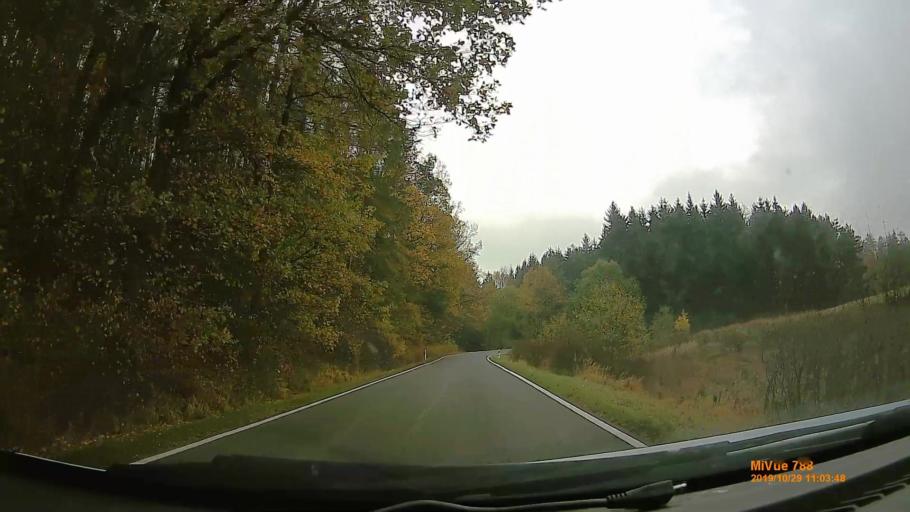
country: PL
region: Lower Silesian Voivodeship
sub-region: Powiat klodzki
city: Radkow
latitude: 50.4820
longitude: 16.4677
